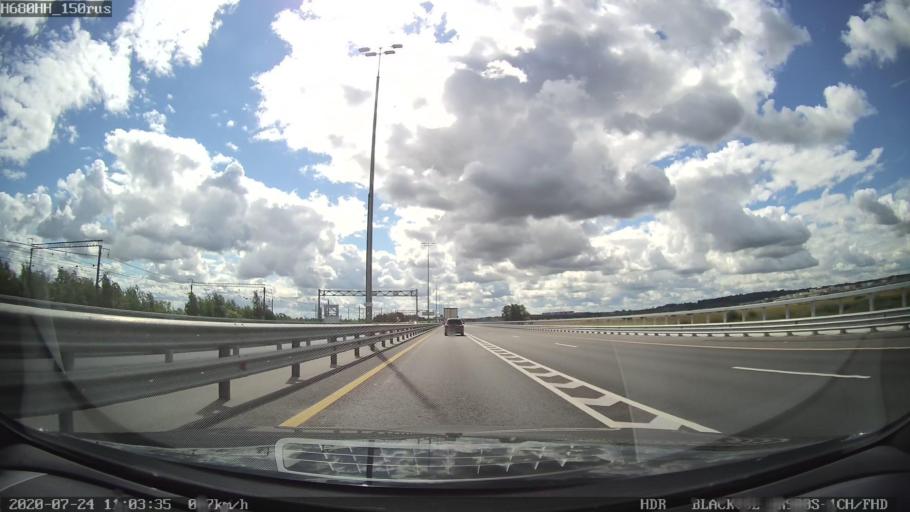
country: RU
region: St.-Petersburg
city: Shushary
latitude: 59.8007
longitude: 30.3391
